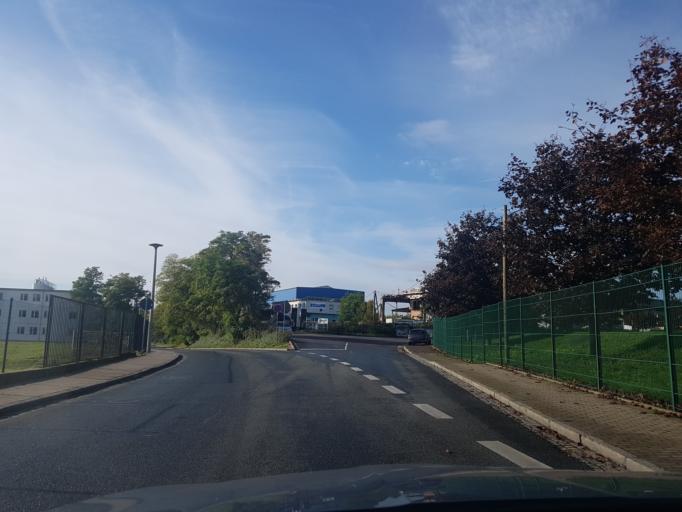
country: DE
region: Saxony
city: Riesa
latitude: 51.3004
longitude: 13.2929
